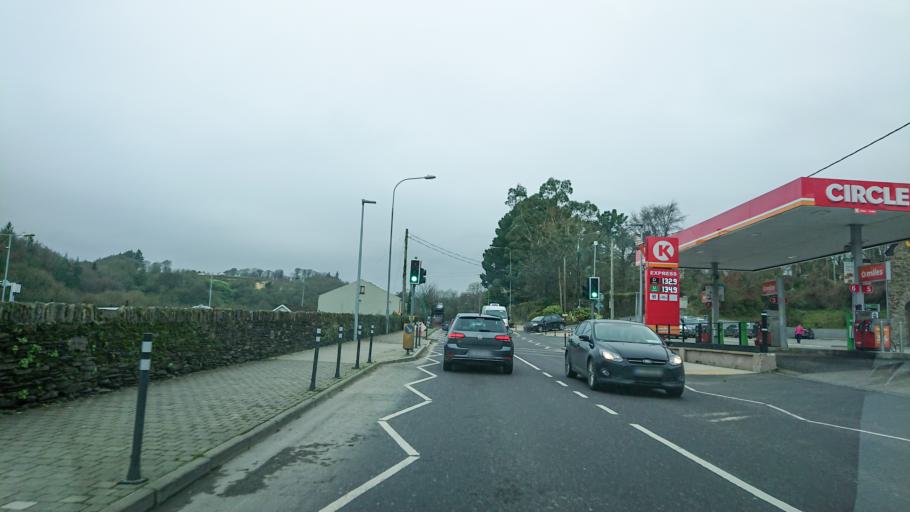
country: IE
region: Munster
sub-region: County Cork
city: Bandon
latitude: 51.7652
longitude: -8.6603
